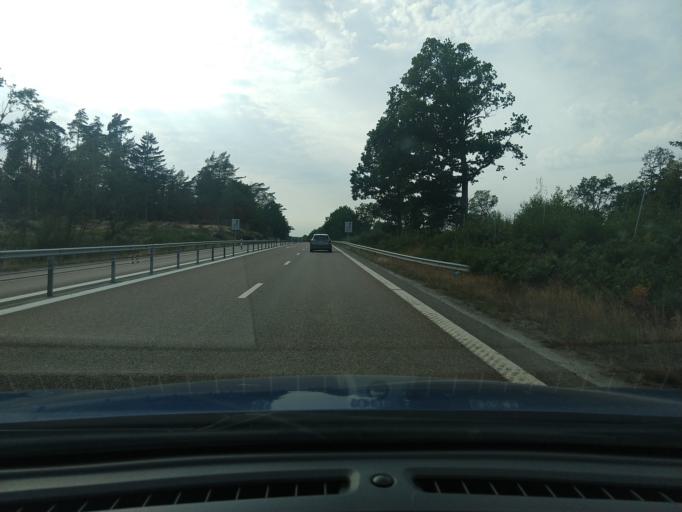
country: SE
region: Blekinge
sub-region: Ronneby Kommun
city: Kallinge
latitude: 56.2032
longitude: 15.3538
